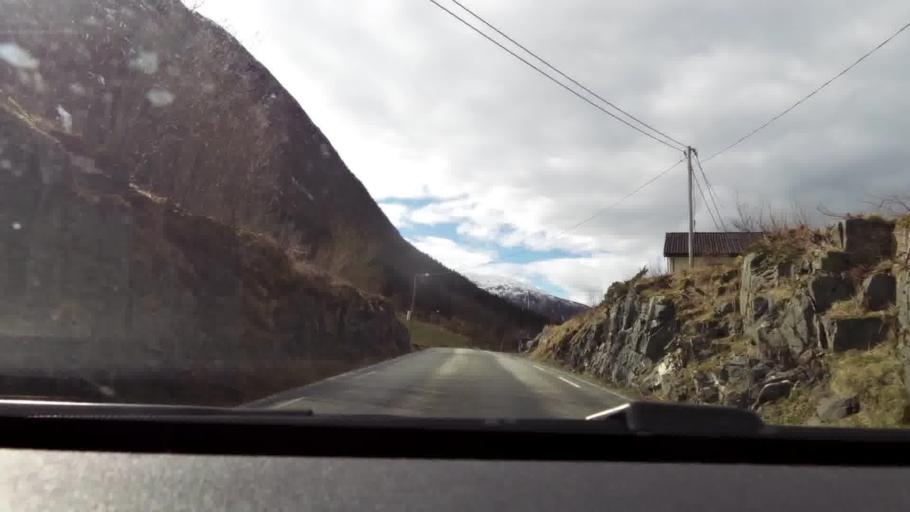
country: NO
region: More og Romsdal
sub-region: Gjemnes
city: Batnfjordsora
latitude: 62.9241
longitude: 7.5690
